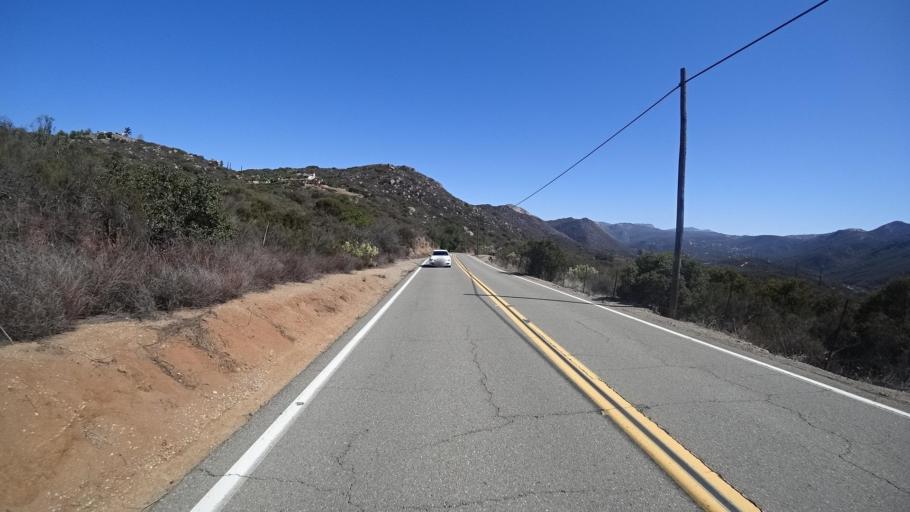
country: US
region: California
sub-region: San Diego County
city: Alpine
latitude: 32.8023
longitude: -116.7678
